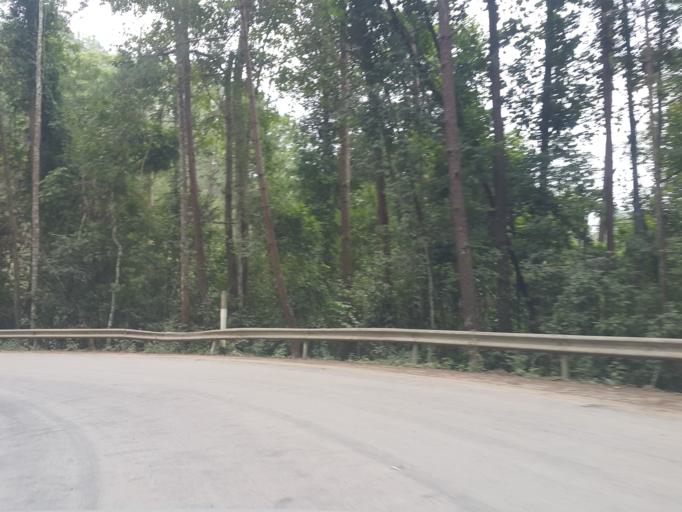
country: TH
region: Mae Hong Son
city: Mae Hi
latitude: 19.2509
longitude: 98.6490
